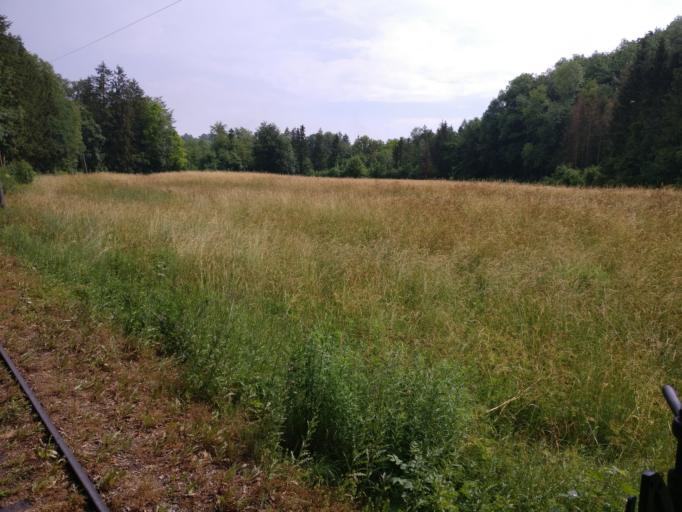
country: AT
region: Upper Austria
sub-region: Politischer Bezirk Steyr-Land
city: Sierning
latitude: 48.0498
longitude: 14.3399
